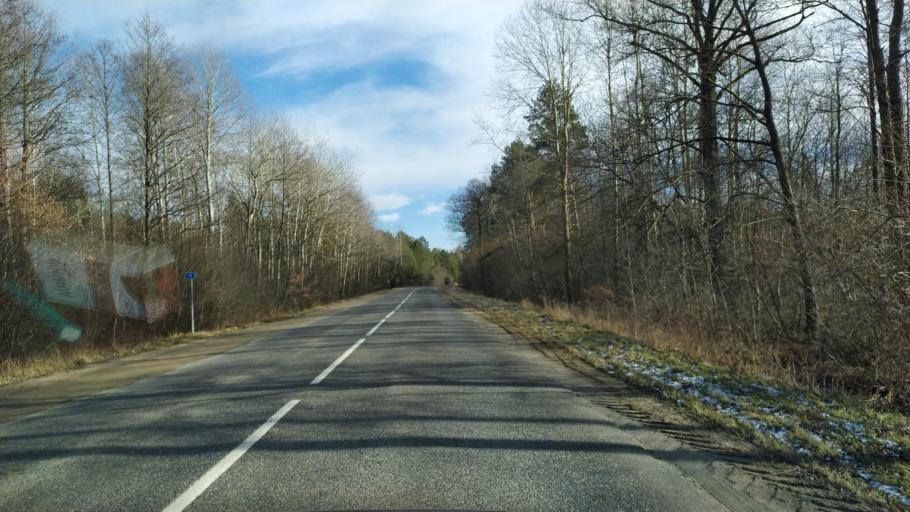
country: BY
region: Brest
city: Pruzhany
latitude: 52.5768
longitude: 24.2971
